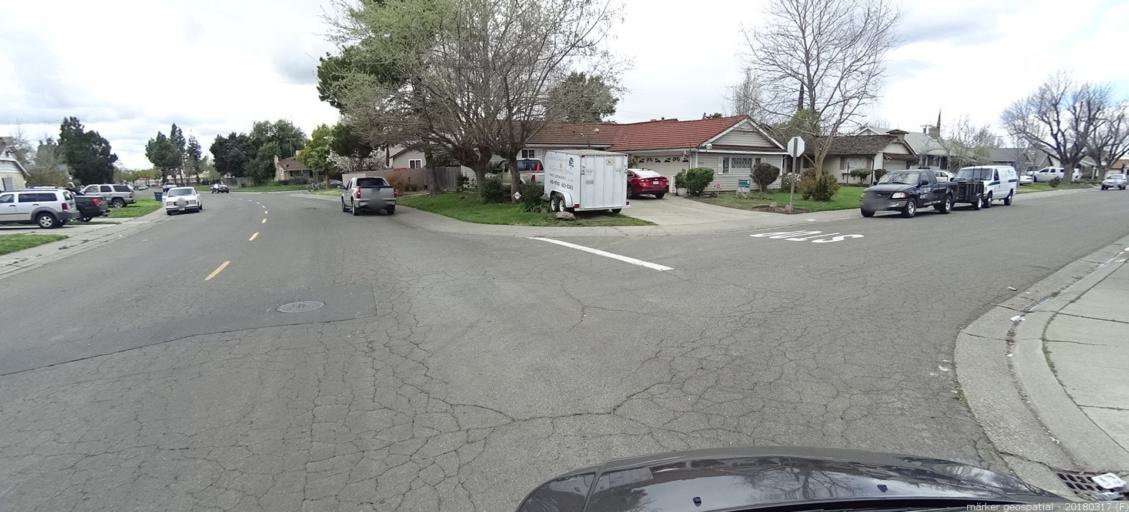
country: US
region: California
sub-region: Sacramento County
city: Parkway
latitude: 38.4998
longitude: -121.4566
